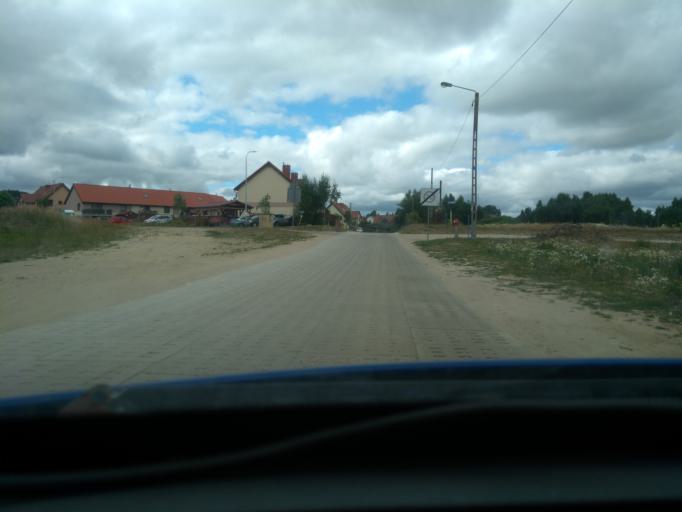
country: PL
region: Pomeranian Voivodeship
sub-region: Powiat kartuski
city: Banino
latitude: 54.3996
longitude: 18.3981
